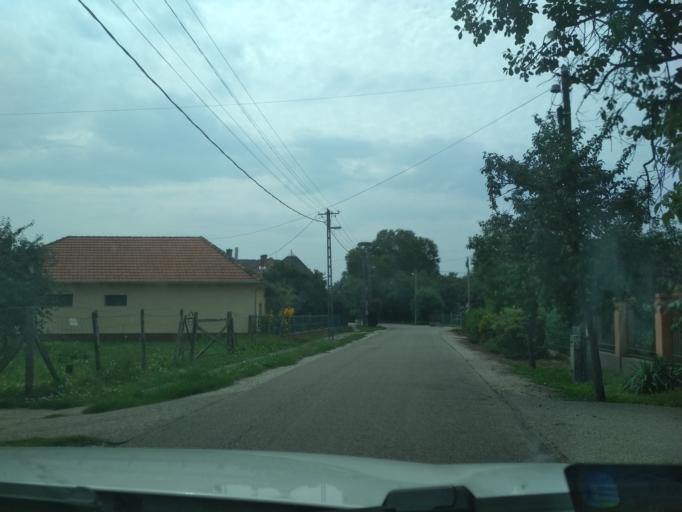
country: HU
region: Jasz-Nagykun-Szolnok
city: Tiszafured
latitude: 47.6225
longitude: 20.7572
